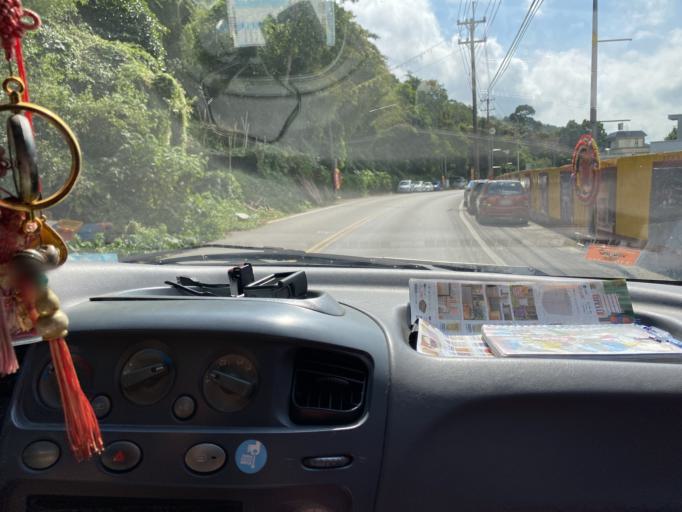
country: TW
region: Taiwan
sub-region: Hsinchu
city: Zhubei
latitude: 24.7395
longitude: 121.1326
